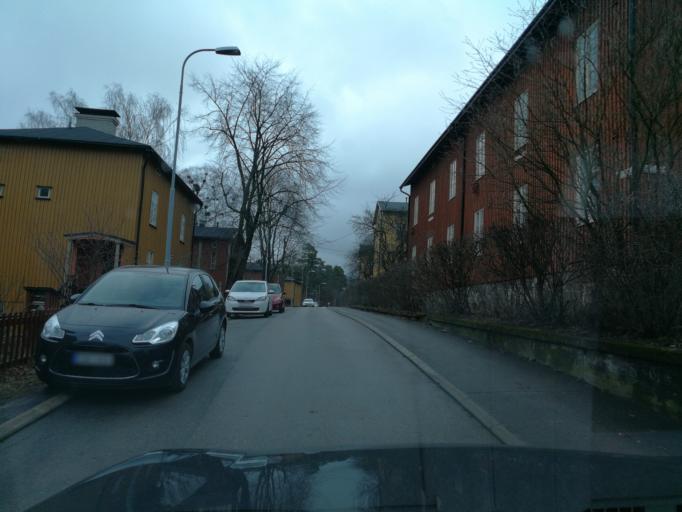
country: FI
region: Uusimaa
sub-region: Helsinki
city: Helsinki
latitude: 60.2142
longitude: 24.9507
